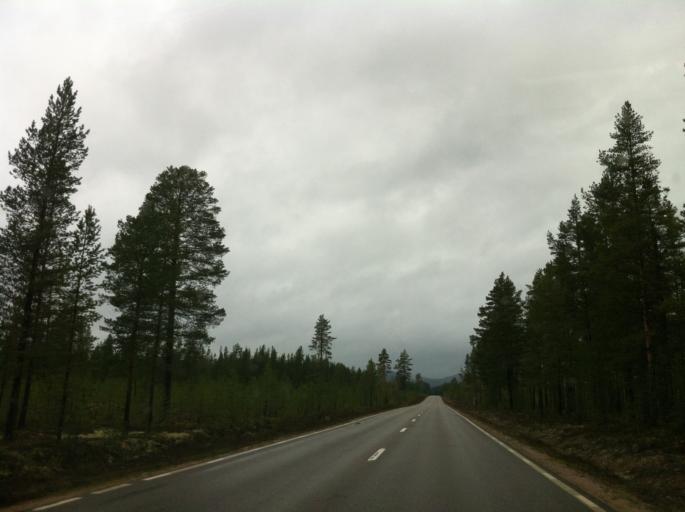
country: SE
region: Jaemtland
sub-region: Harjedalens Kommun
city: Sveg
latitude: 62.1374
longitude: 13.9947
